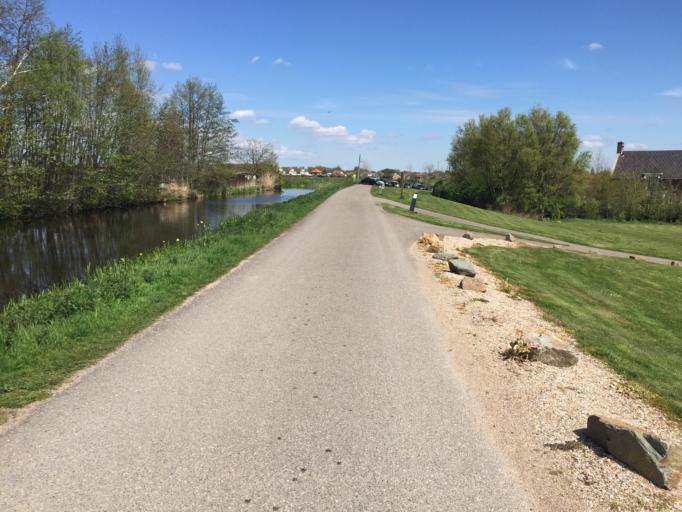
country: NL
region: South Holland
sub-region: Gemeente Nieuwkoop
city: Nieuwkoop
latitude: 52.1905
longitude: 4.7428
